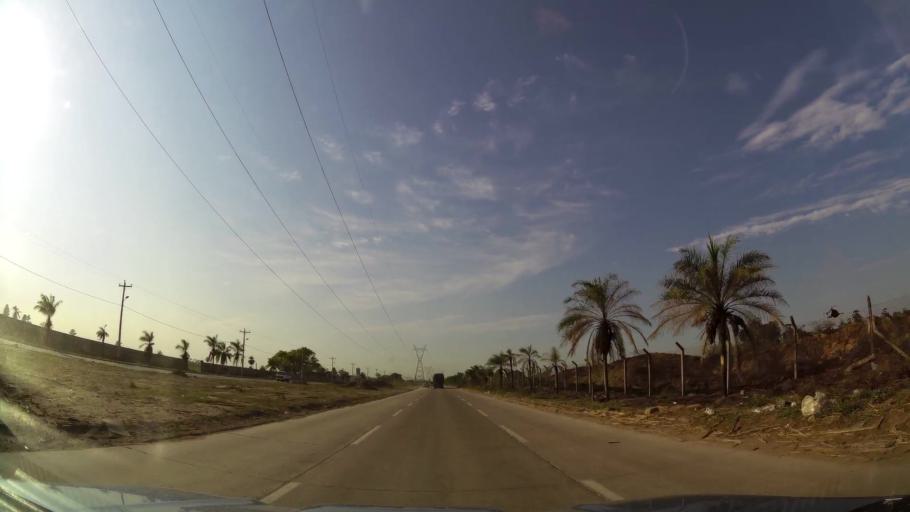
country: BO
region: Santa Cruz
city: Santa Cruz de la Sierra
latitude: -17.6966
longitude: -63.1366
